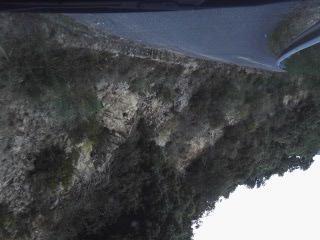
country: IT
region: Calabria
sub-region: Provincia di Vibo-Valentia
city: Nardodipace
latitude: 38.4398
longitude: 16.3394
